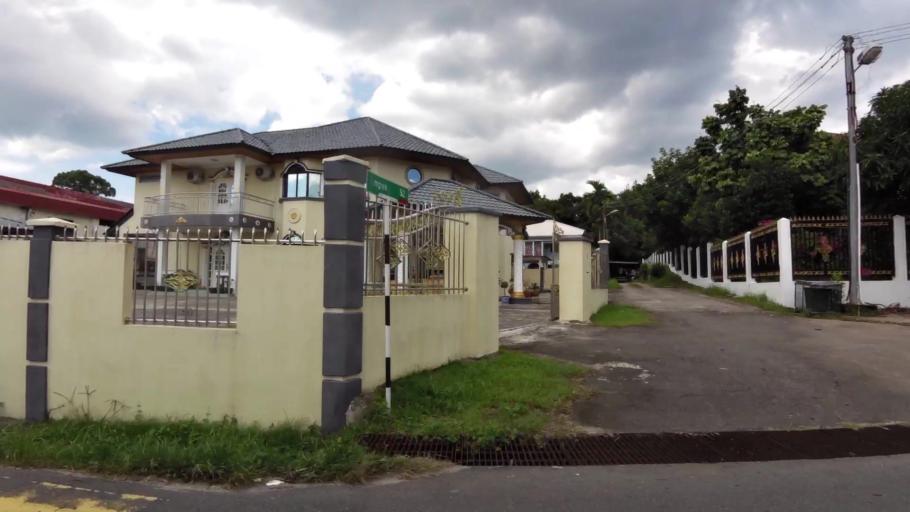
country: BN
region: Brunei and Muara
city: Bandar Seri Begawan
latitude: 4.9544
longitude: 114.9642
